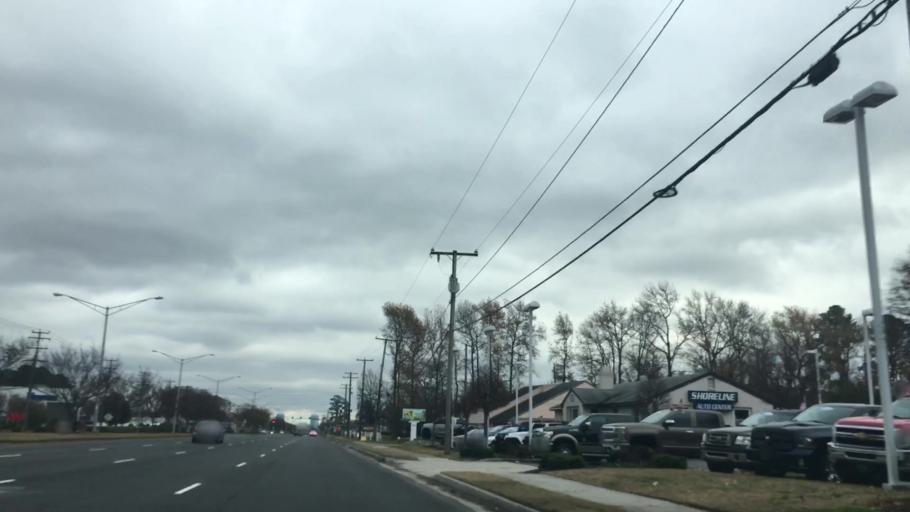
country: US
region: Virginia
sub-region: City of Chesapeake
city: Chesapeake
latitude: 36.8502
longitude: -76.1680
